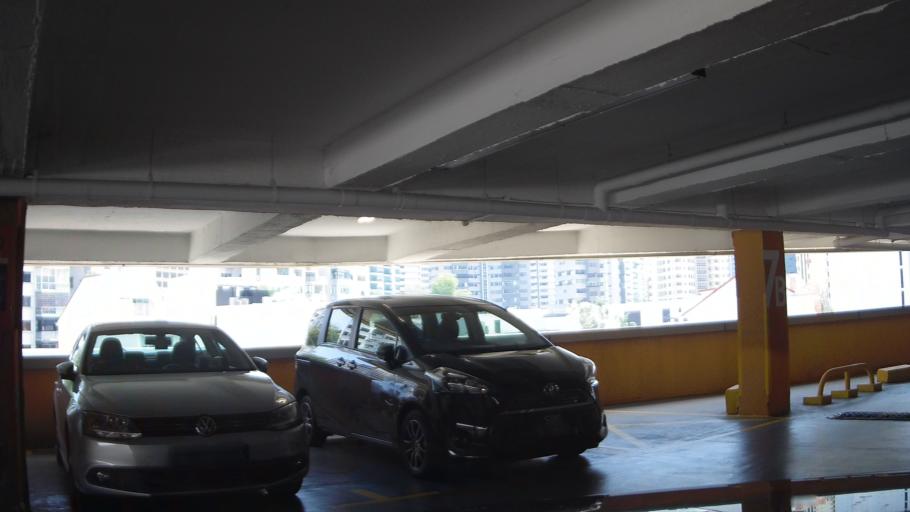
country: SG
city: Singapore
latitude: 1.2618
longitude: 103.8426
